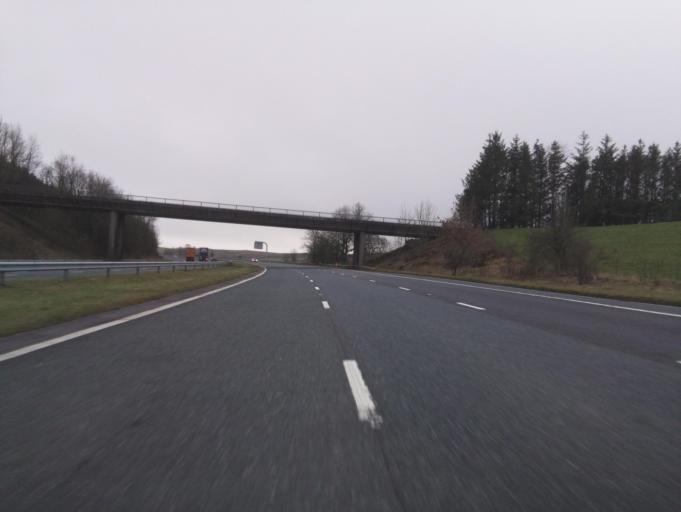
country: GB
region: England
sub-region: Cumbria
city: Sedbergh
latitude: 54.3535
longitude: -2.6203
